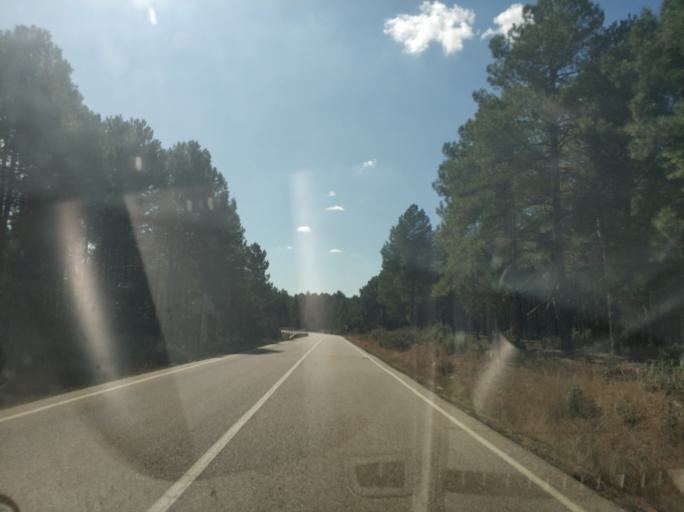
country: ES
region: Castille and Leon
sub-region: Provincia de Soria
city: Ucero
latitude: 41.7445
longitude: -3.0443
